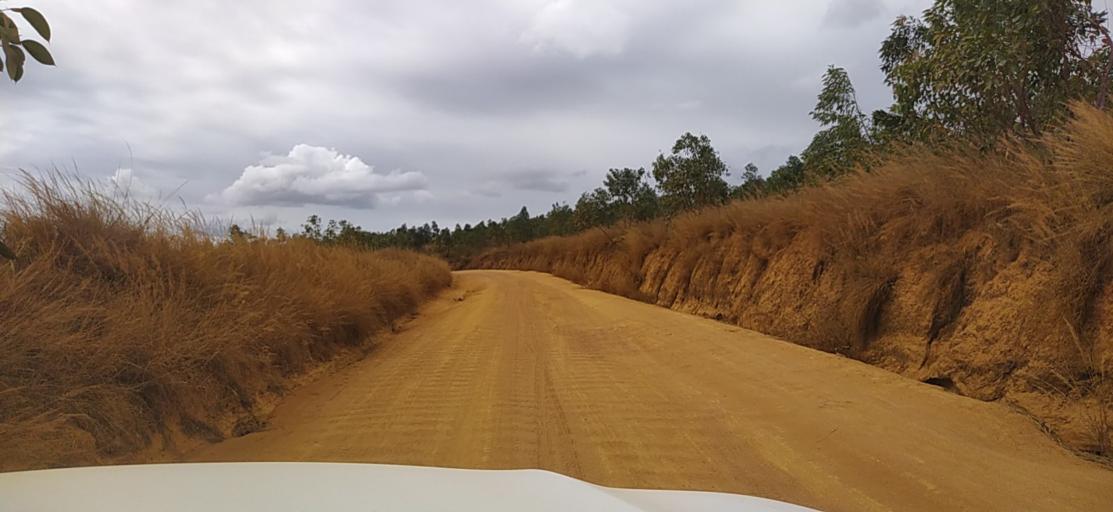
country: MG
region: Alaotra Mangoro
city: Ambatondrazaka
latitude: -17.9513
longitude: 48.2489
